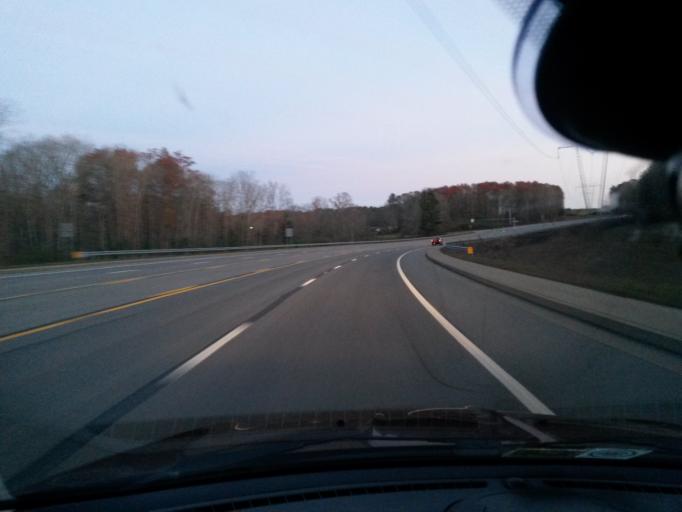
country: US
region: West Virginia
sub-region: Raleigh County
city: Stanaford
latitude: 37.7875
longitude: -81.1551
